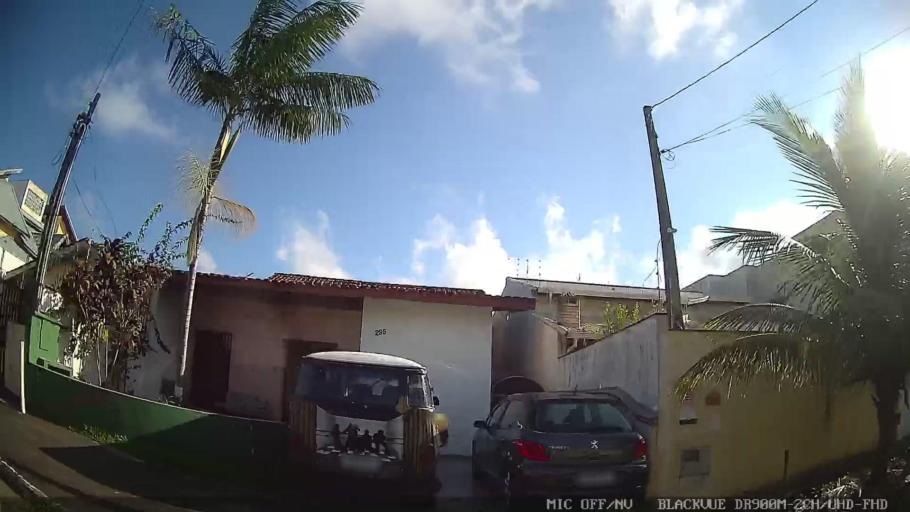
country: BR
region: Sao Paulo
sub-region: Peruibe
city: Peruibe
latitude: -24.2926
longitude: -46.9632
